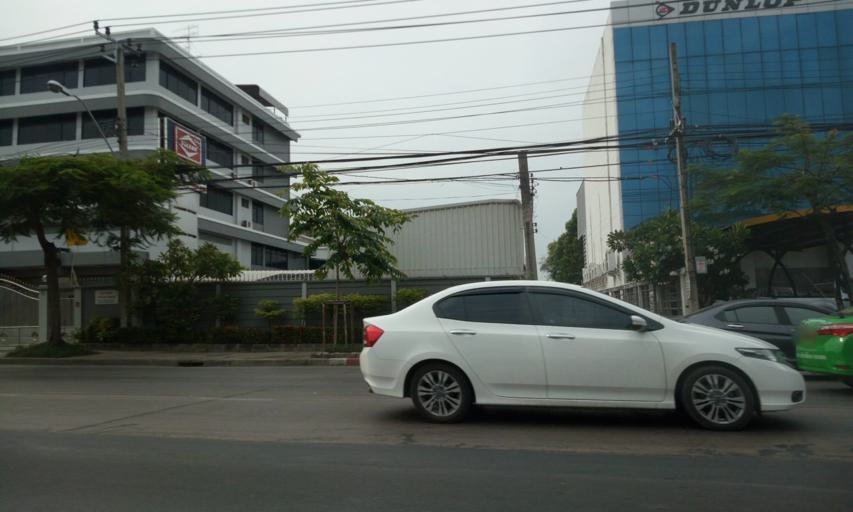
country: TH
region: Bangkok
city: Saphan Sung
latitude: 13.7221
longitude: 100.7232
